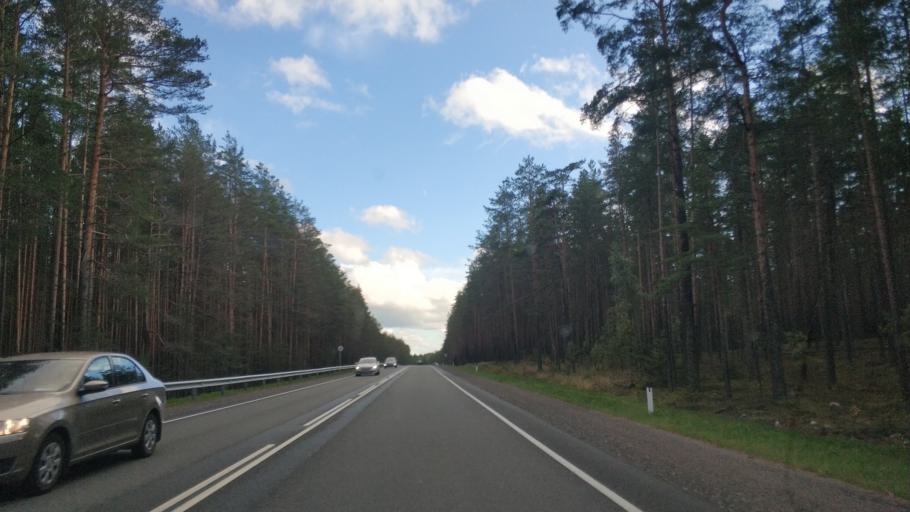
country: RU
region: Leningrad
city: Priozersk
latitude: 60.9919
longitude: 30.1833
